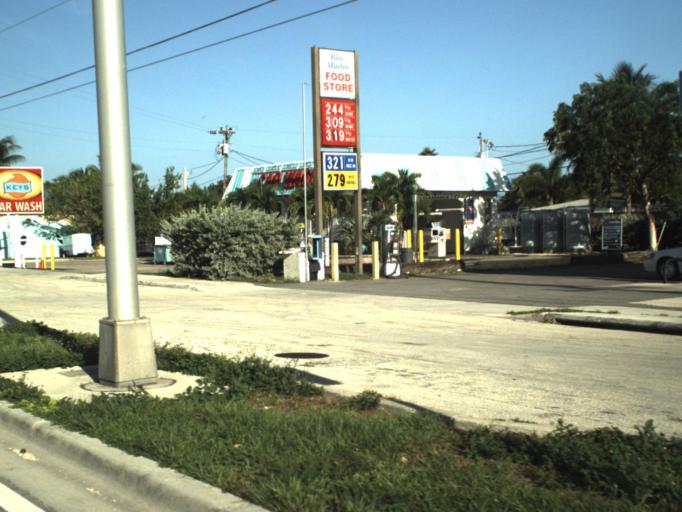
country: US
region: Florida
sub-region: Monroe County
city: Marathon
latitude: 24.7289
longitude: -81.0365
